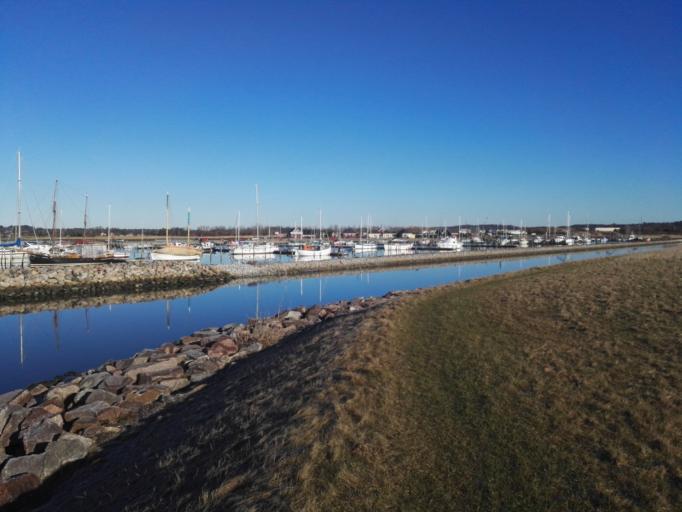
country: DK
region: Capital Region
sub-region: Halsnaes Kommune
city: Frederiksvaerk
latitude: 55.9623
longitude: 11.9984
